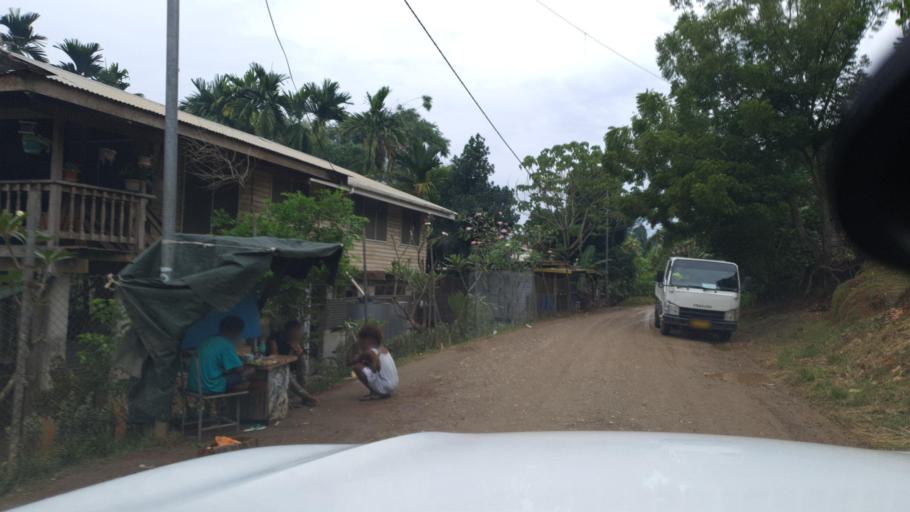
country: SB
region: Guadalcanal
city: Honiara
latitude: -9.4464
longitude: 159.9794
